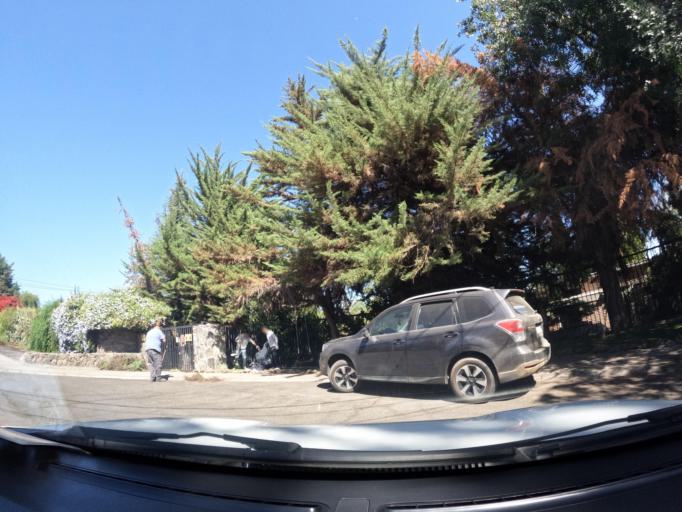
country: CL
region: Santiago Metropolitan
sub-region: Provincia de Santiago
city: Villa Presidente Frei, Nunoa, Santiago, Chile
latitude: -33.4714
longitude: -70.5230
